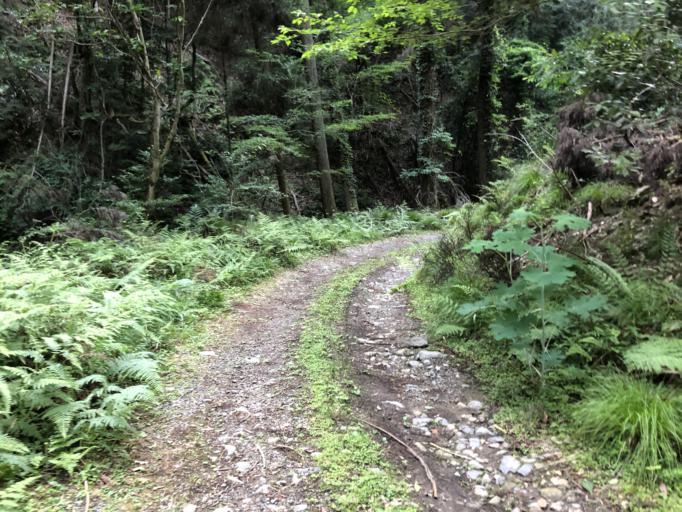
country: JP
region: Kyoto
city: Kameoka
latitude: 34.9866
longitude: 135.6237
